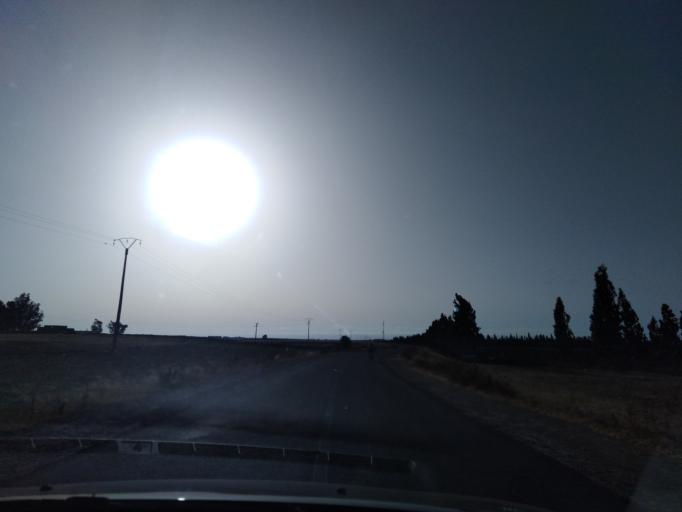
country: MA
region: Doukkala-Abda
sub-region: Safi
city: Safi
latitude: 32.4818
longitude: -8.9093
